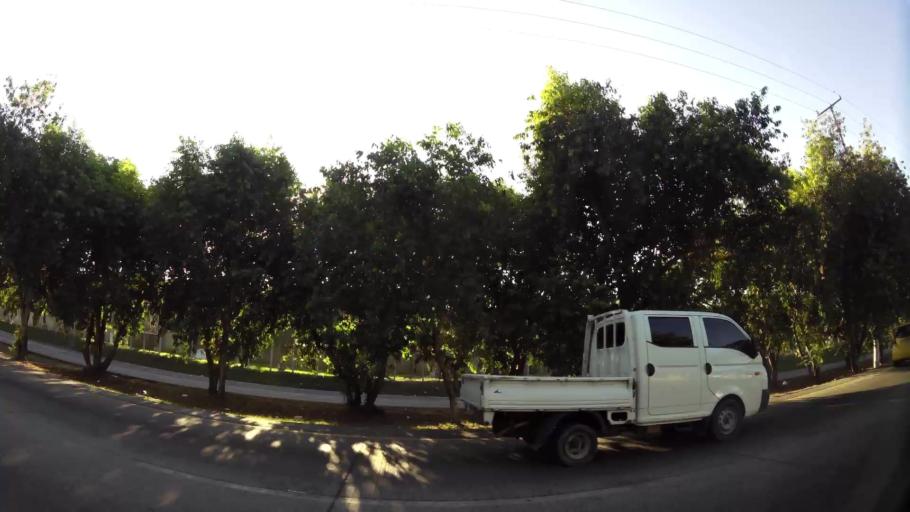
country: SV
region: La Libertad
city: Santa Tecla
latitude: 13.7475
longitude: -89.3643
